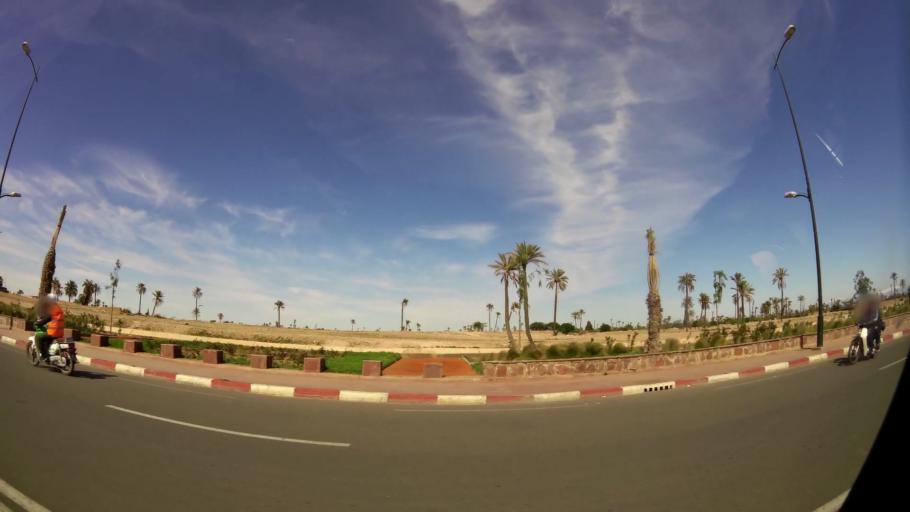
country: MA
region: Marrakech-Tensift-Al Haouz
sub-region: Marrakech
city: Marrakesh
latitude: 31.6313
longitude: -7.9737
